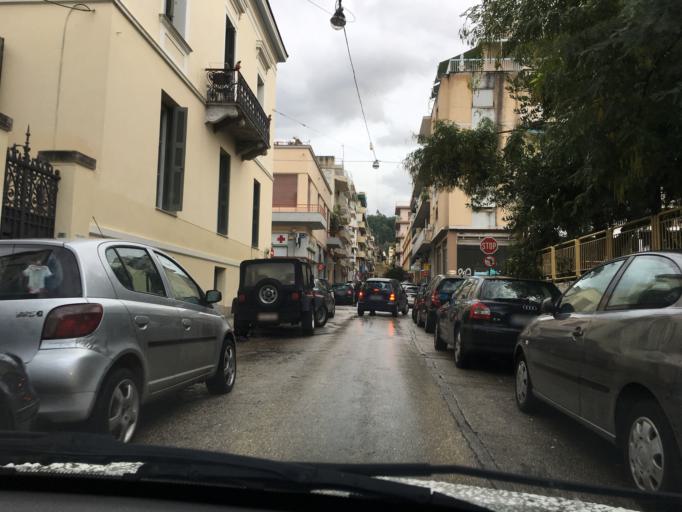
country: GR
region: West Greece
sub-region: Nomos Achaias
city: Patra
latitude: 38.2510
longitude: 21.7387
